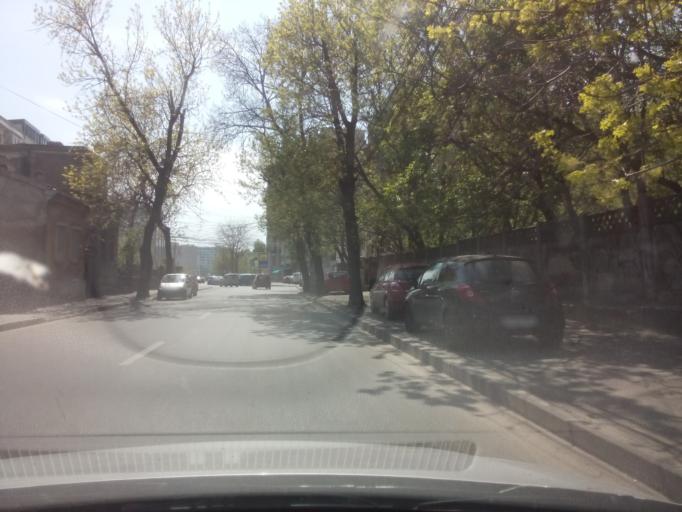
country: RO
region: Bucuresti
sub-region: Municipiul Bucuresti
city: Bucharest
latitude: 44.4284
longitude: 26.1192
